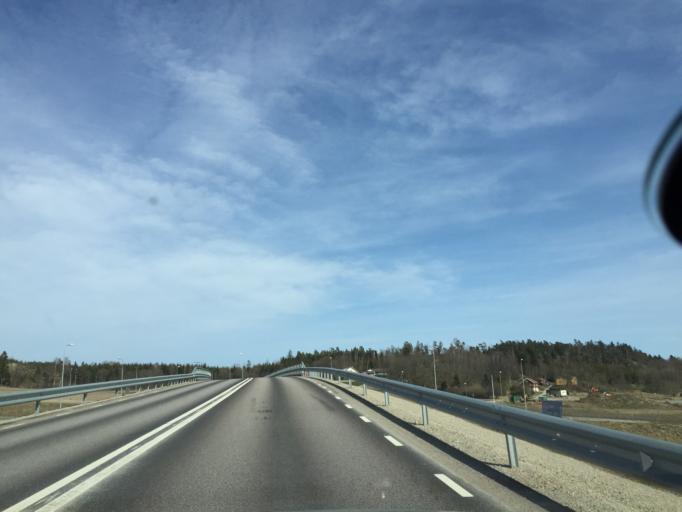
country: SE
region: Vaestra Goetaland
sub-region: Uddevalla Kommun
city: Uddevalla
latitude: 58.3570
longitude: 11.8118
